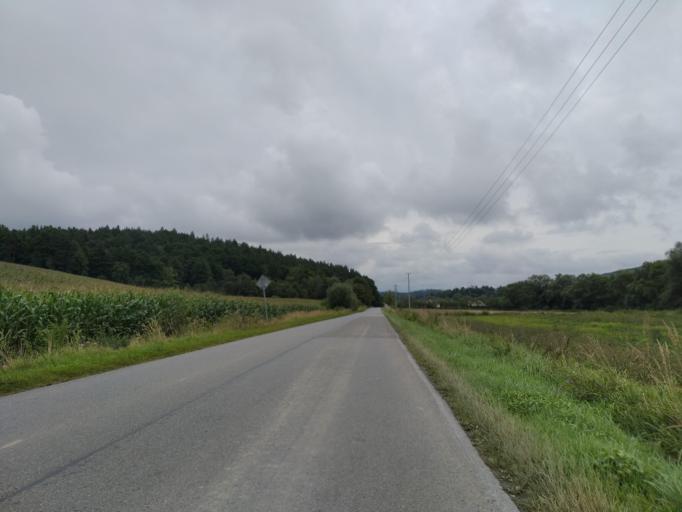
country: PL
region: Subcarpathian Voivodeship
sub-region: Powiat przemyski
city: Bircza
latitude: 49.6899
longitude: 22.3945
